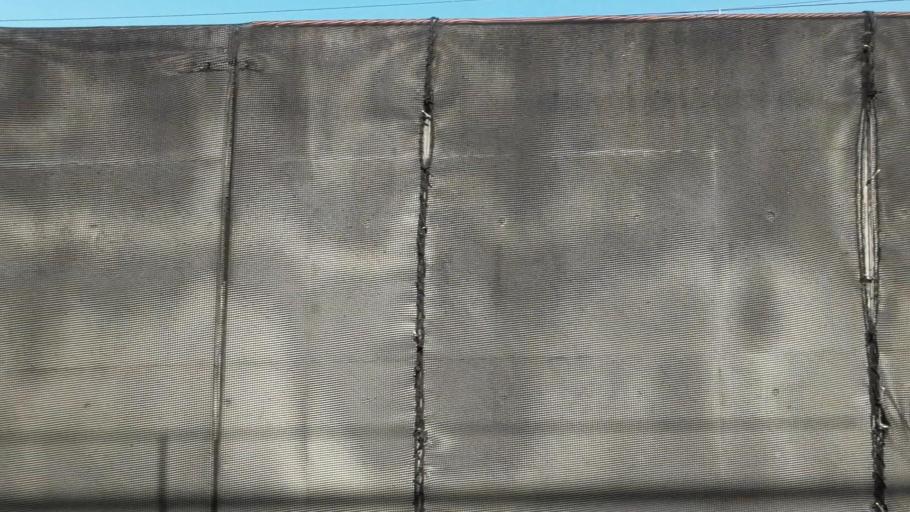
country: JP
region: Kagawa
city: Sakaidecho
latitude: 34.3091
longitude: 133.8157
